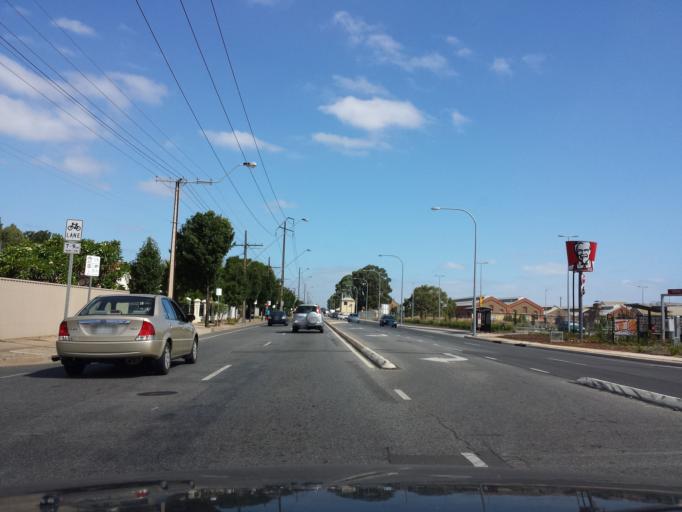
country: AU
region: South Australia
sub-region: Port Adelaide Enfield
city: Blair Athol
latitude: -34.8656
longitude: 138.5835
